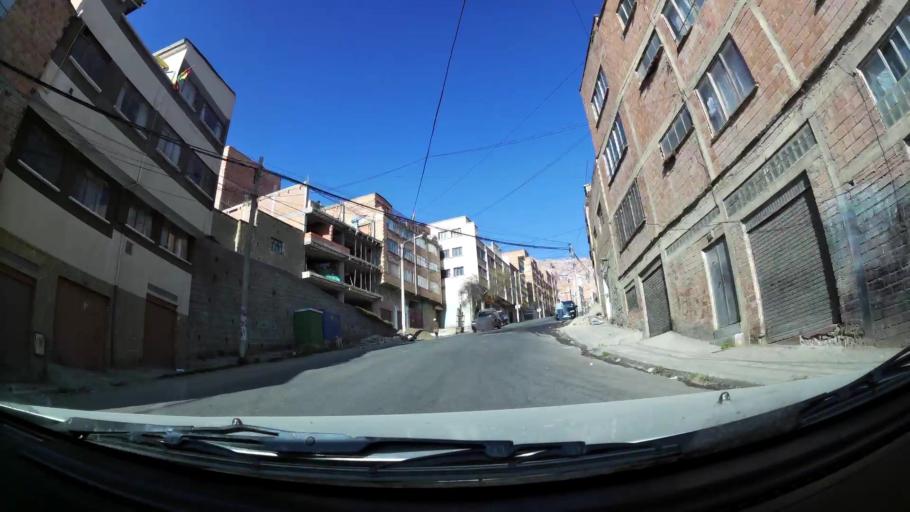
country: BO
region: La Paz
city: La Paz
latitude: -16.5016
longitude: -68.1466
